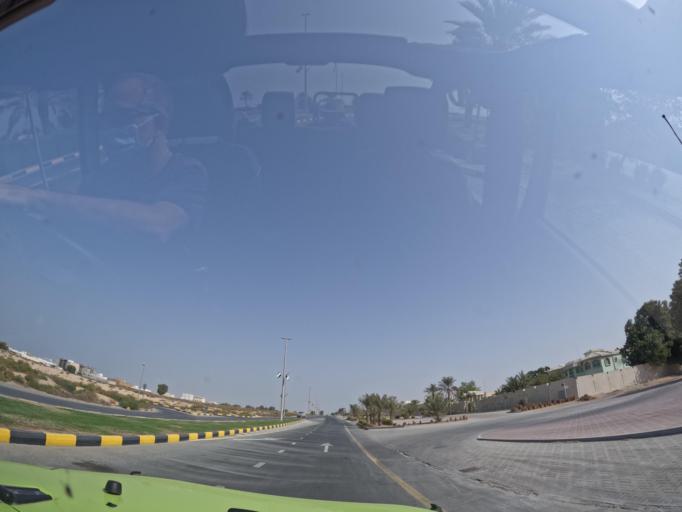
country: AE
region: Umm al Qaywayn
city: Umm al Qaywayn
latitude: 25.4757
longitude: 55.5287
